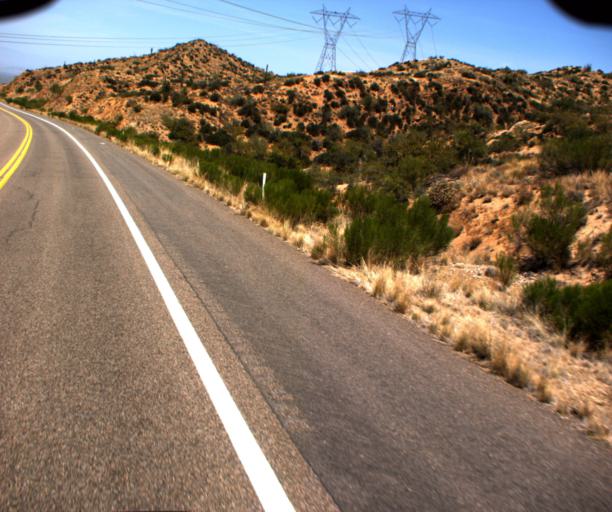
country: US
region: Arizona
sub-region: Gila County
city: Miami
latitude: 33.5445
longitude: -110.9400
